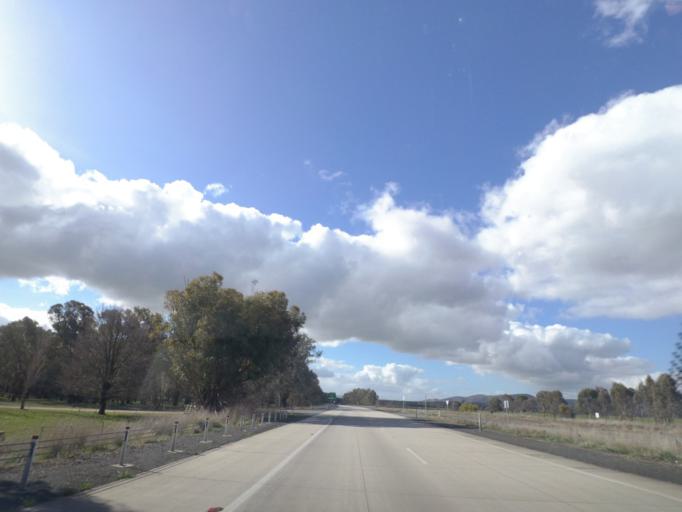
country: AU
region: New South Wales
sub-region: Greater Hume Shire
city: Holbrook
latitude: -35.7499
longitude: 147.2971
